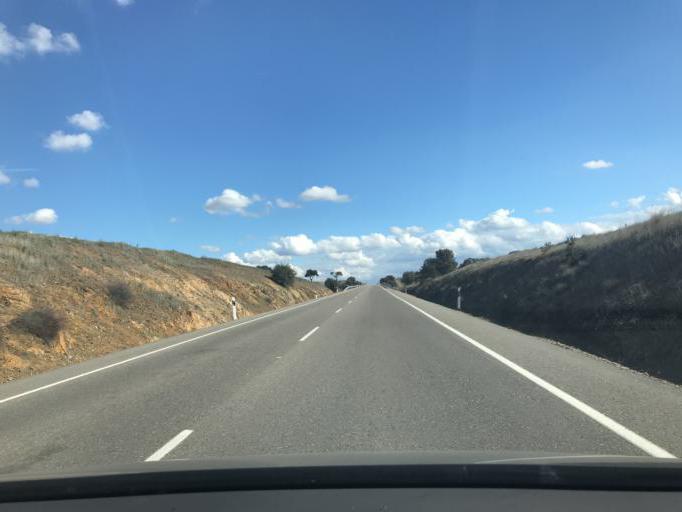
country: ES
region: Extremadura
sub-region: Provincia de Badajoz
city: Granja de Torrehermosa
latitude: 38.2934
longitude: -5.5411
